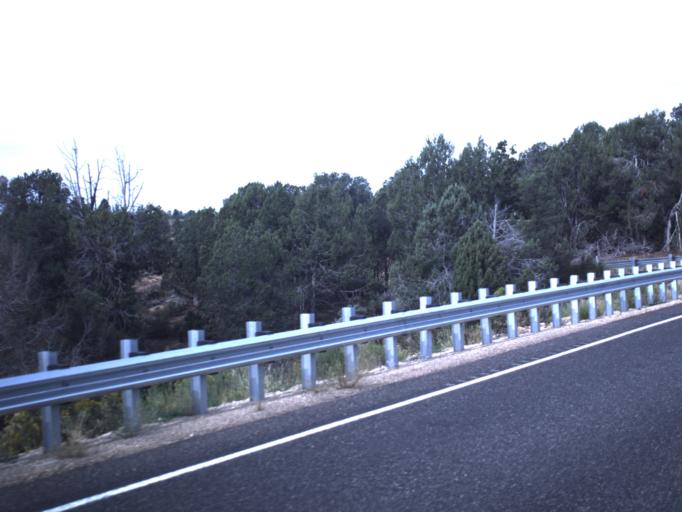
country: US
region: Utah
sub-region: Kane County
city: Kanab
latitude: 37.2223
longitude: -112.7146
